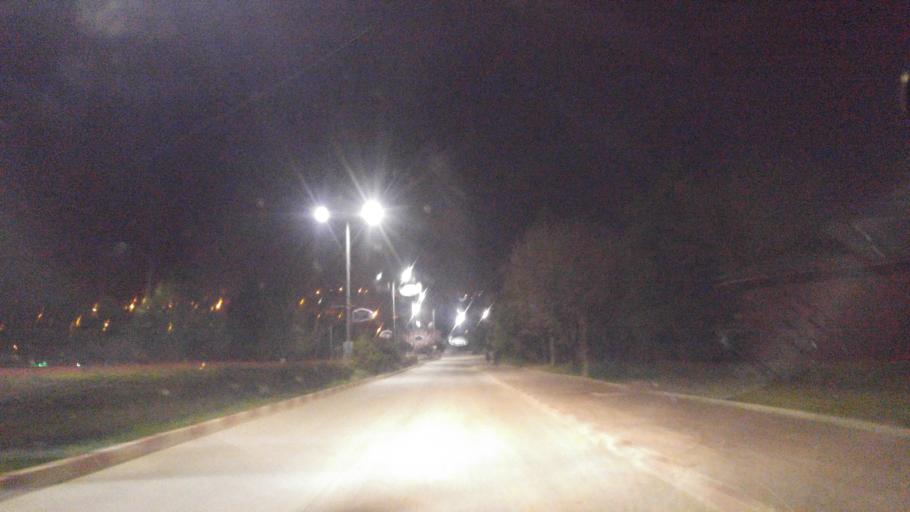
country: TR
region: Karabuk
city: Karabuk
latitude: 41.2120
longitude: 32.6540
